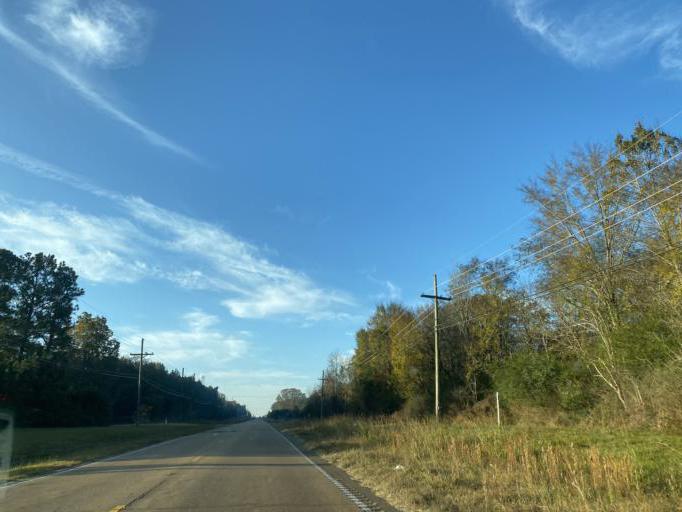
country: US
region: Mississippi
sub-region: Madison County
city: Madison
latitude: 32.4988
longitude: -90.0922
